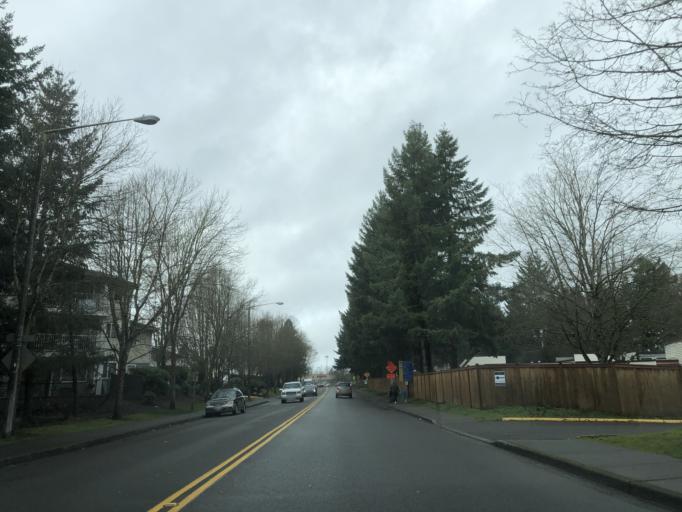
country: US
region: Washington
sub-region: King County
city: Fairwood
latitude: 47.4450
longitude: -122.1451
